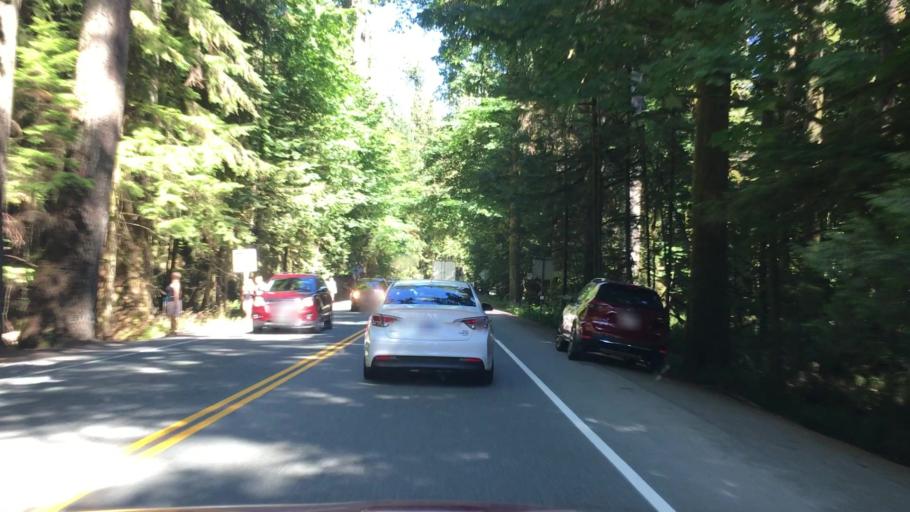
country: CA
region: British Columbia
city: Port Alberni
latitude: 49.2912
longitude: -124.6625
